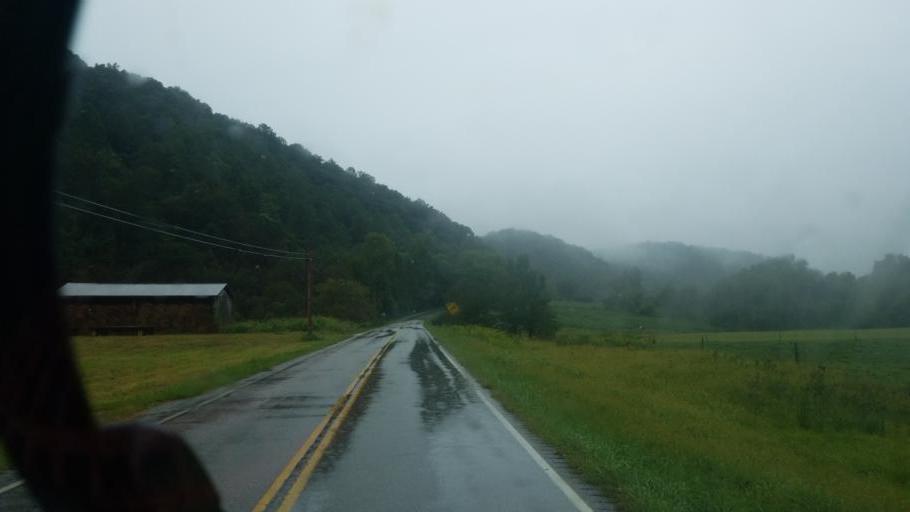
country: US
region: Kentucky
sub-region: Greenup County
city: South Shore
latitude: 38.6889
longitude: -82.9345
